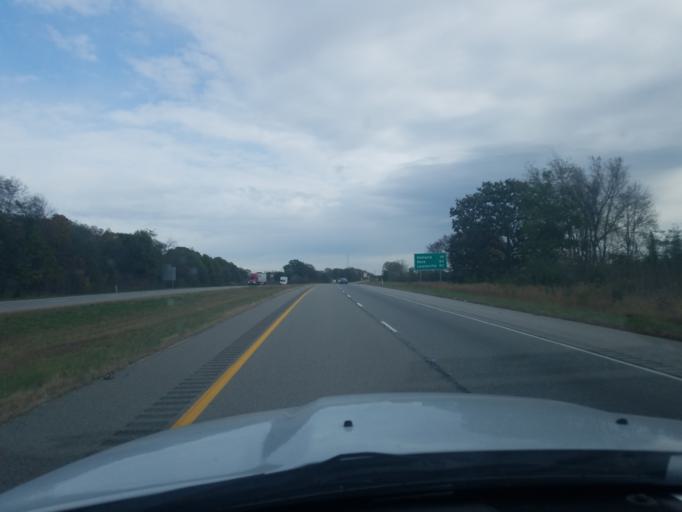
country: US
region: Indiana
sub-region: Warrick County
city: Boonville
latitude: 38.1984
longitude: -87.2808
